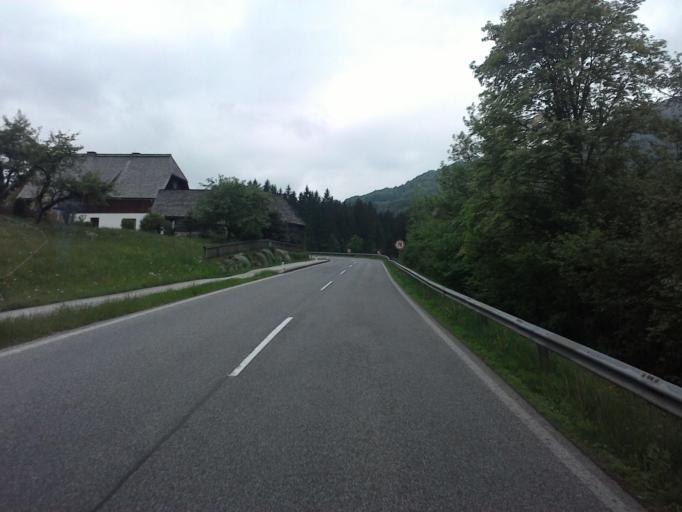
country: AT
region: Styria
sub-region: Politischer Bezirk Liezen
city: Landl
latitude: 47.6654
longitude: 14.7295
